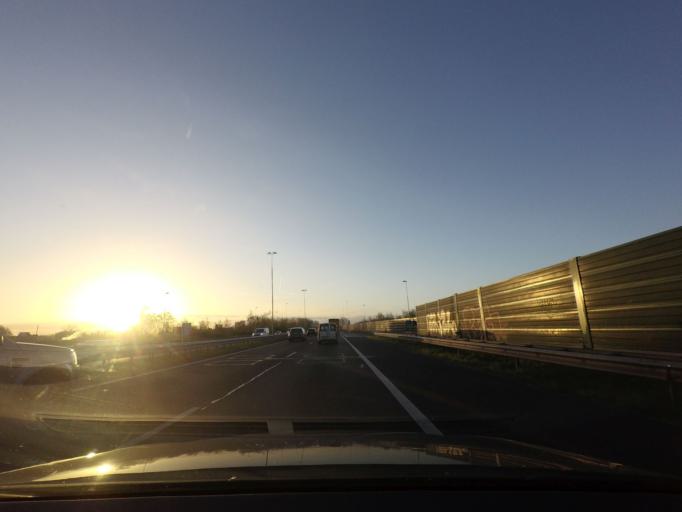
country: NL
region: North Holland
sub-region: Gemeente Zaanstad
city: Zaanstad
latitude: 52.4658
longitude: 4.7999
